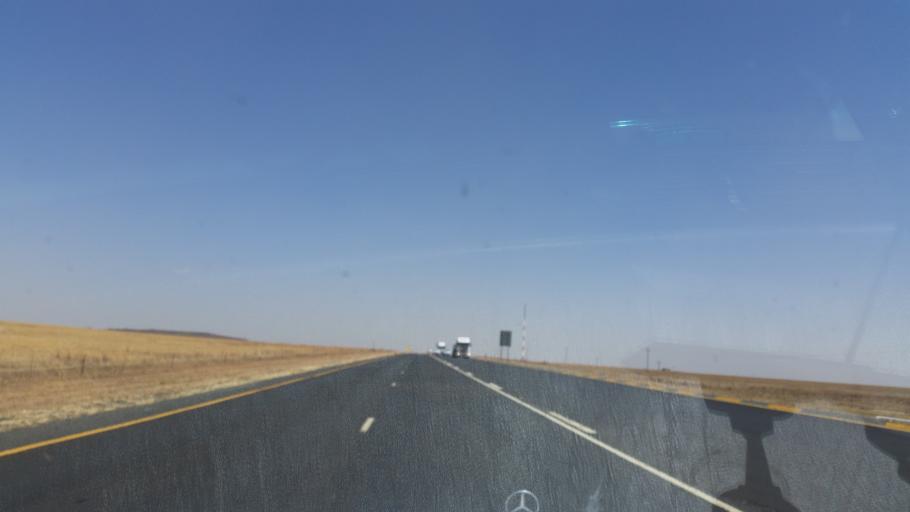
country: ZA
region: Orange Free State
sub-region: Lejweleputswa District Municipality
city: Brandfort
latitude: -28.8097
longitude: 26.6762
